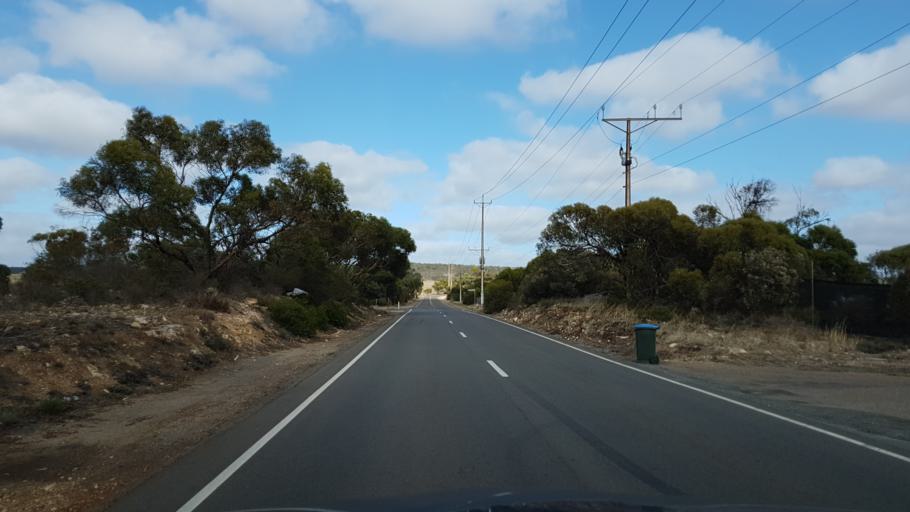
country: AU
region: South Australia
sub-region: Murray Bridge
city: Murray Bridge
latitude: -35.1171
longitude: 139.2442
